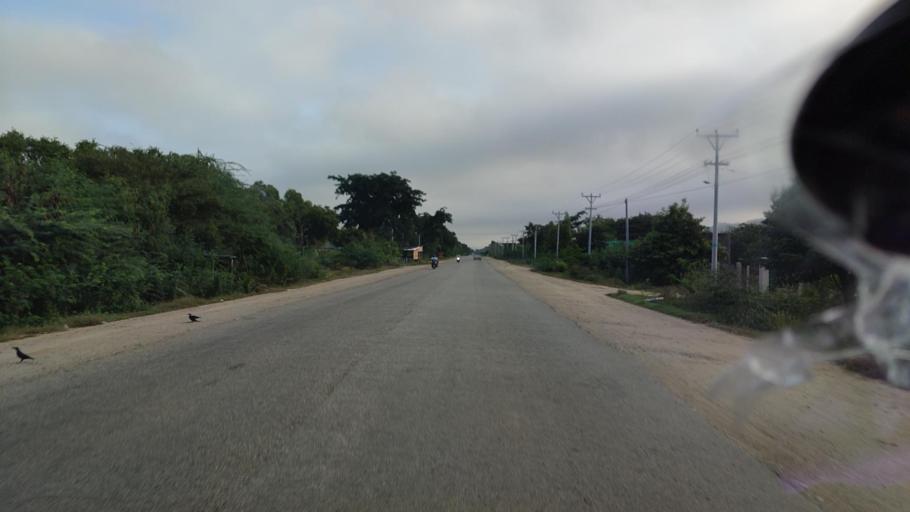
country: MM
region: Mandalay
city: Yamethin
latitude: 20.7134
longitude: 96.1847
